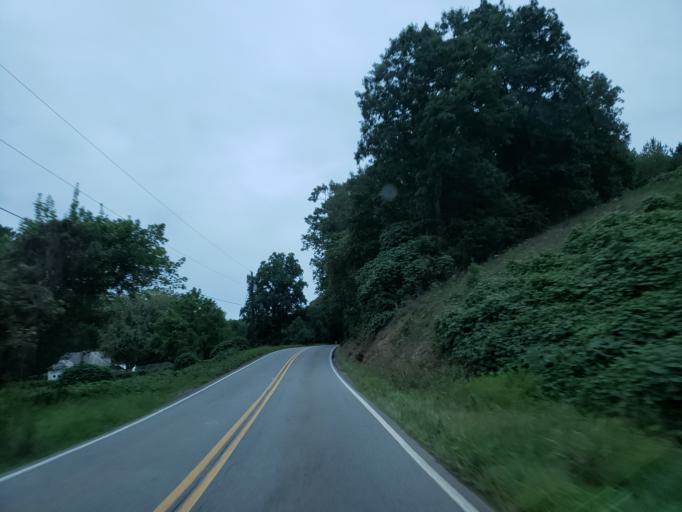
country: US
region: Georgia
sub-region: Cherokee County
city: Canton
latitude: 34.2782
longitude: -84.4500
